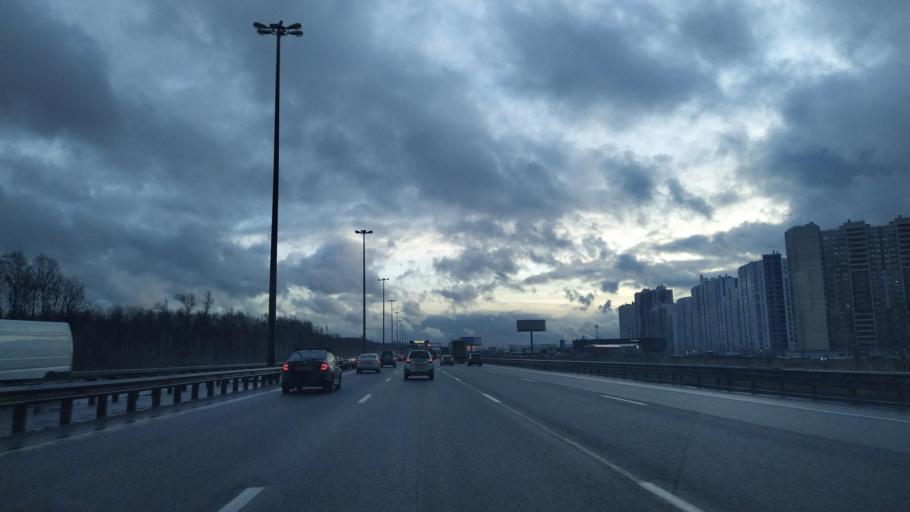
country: RU
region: Leningrad
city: Rybatskoye
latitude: 59.9102
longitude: 30.5244
